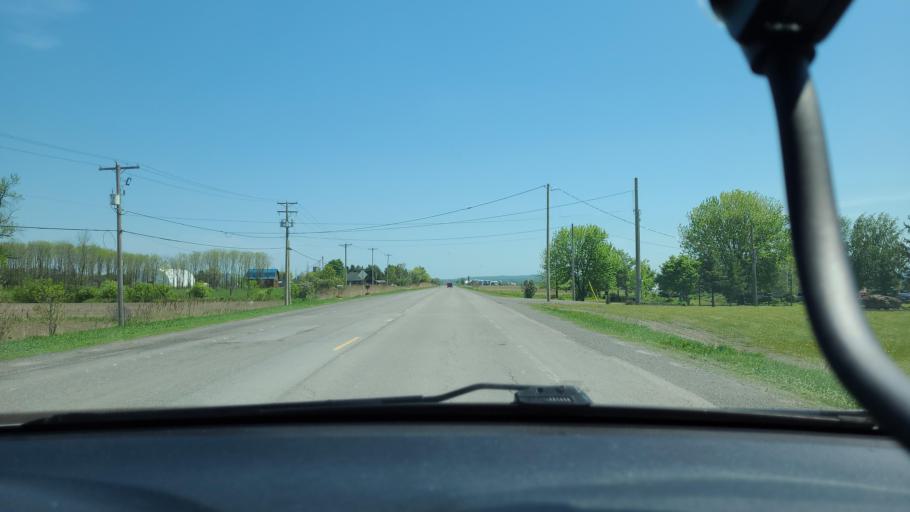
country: CA
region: Quebec
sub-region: Laurentides
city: Mirabel
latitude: 45.6476
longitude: -74.1466
